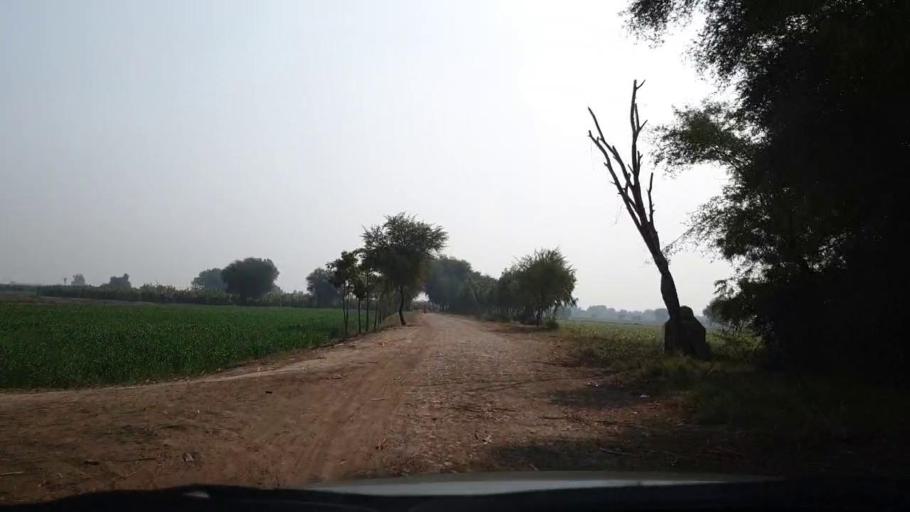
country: PK
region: Sindh
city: Matiari
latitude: 25.6570
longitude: 68.5495
